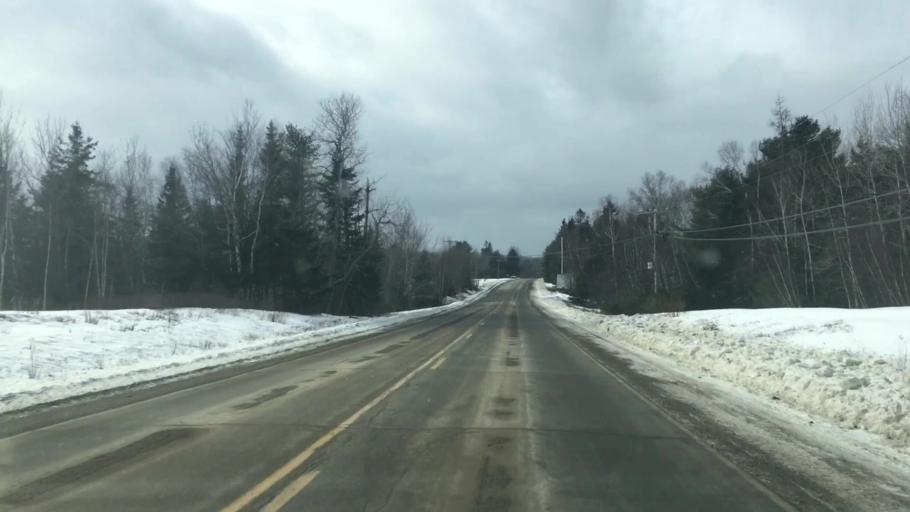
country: US
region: Maine
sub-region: Washington County
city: Calais
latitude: 45.0204
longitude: -67.3811
